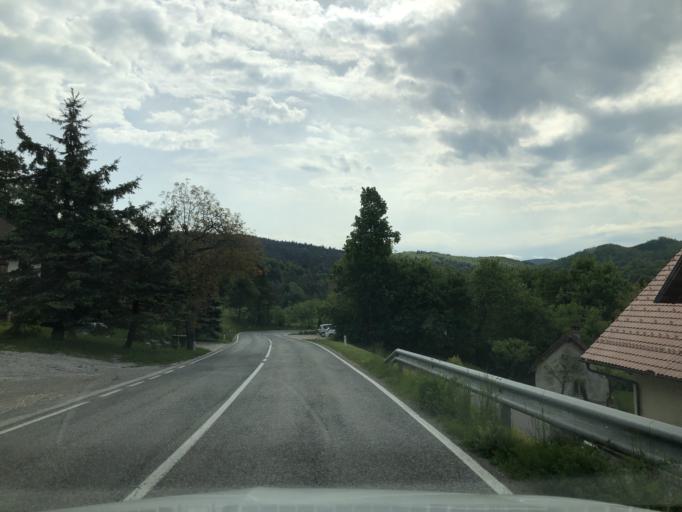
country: SI
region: Bloke
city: Nova Vas
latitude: 45.7621
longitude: 14.4694
